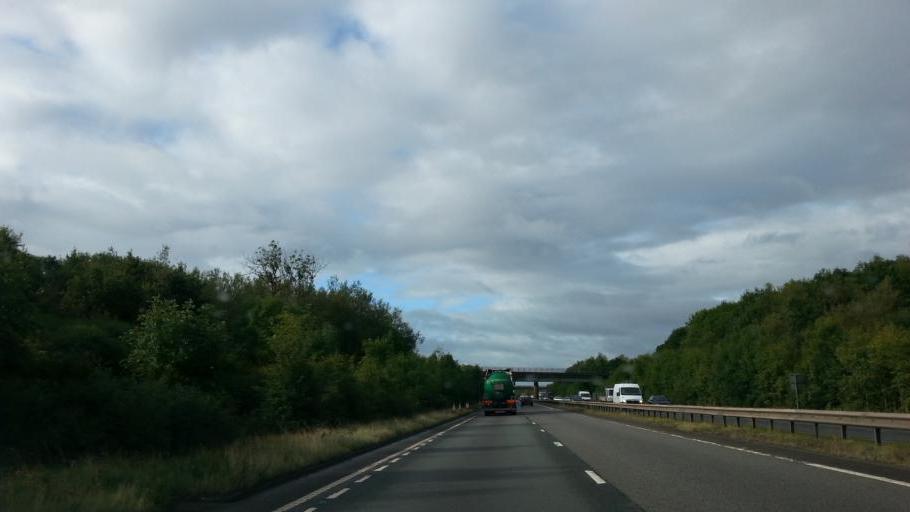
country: GB
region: England
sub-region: Leicestershire
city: Ashby de la Zouch
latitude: 52.7443
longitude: -1.4533
